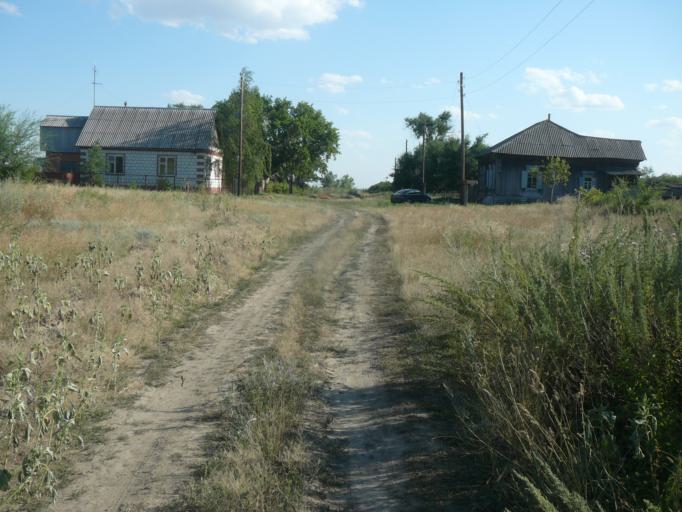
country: RU
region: Saratov
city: Krasnyy Yar
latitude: 51.5593
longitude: 46.5364
